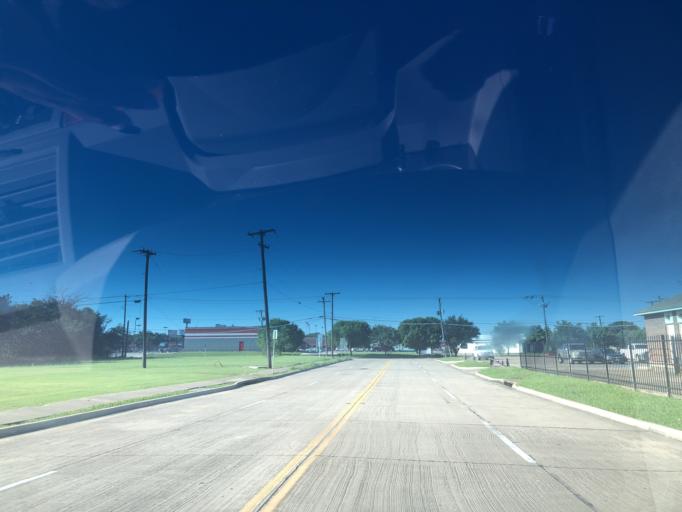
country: US
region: Texas
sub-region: Dallas County
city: Grand Prairie
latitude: 32.7114
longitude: -97.0018
